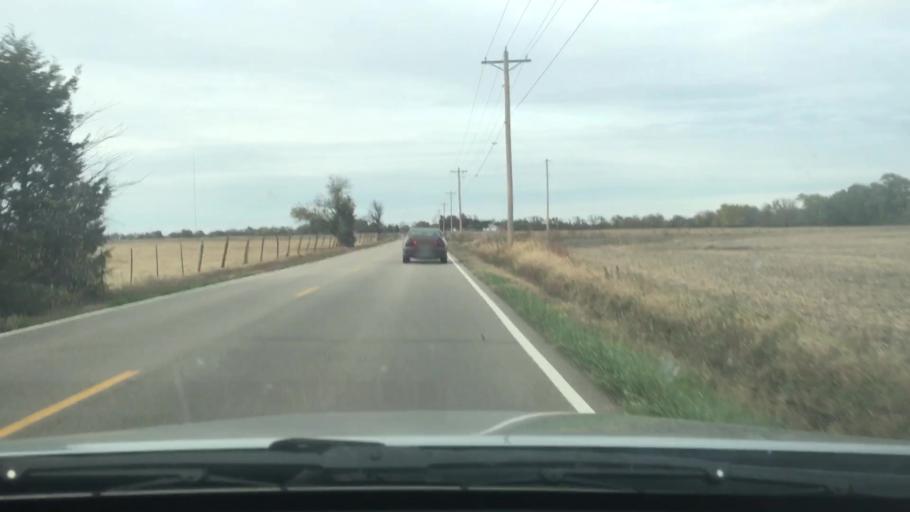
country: US
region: Kansas
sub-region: Sedgwick County
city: Maize
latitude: 37.7441
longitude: -97.4987
